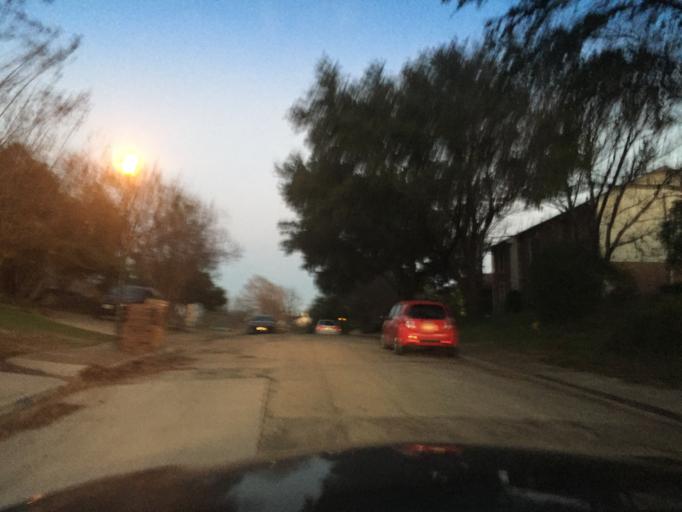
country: US
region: Texas
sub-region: Dallas County
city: Carrollton
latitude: 32.9887
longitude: -96.8976
